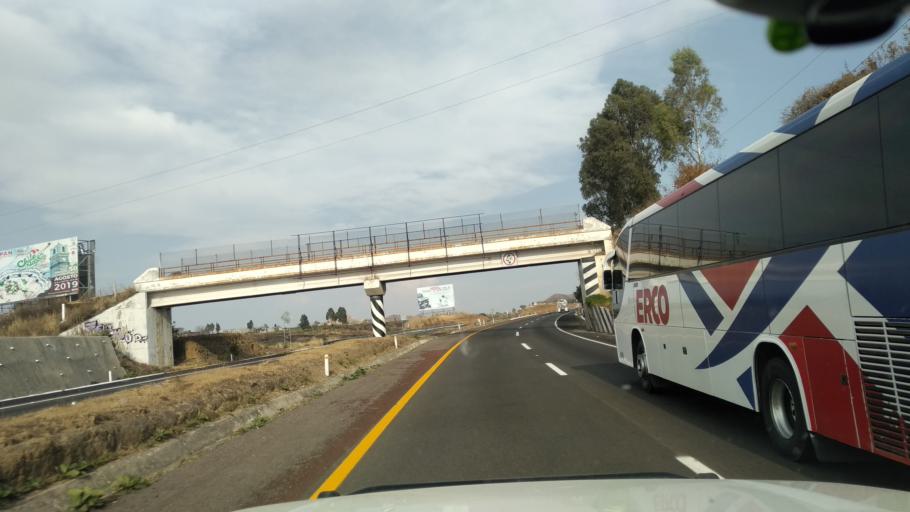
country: MX
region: Puebla
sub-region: Santa Isabel Cholula
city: San Pablo Ahuatempa
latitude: 18.9774
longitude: -98.3582
